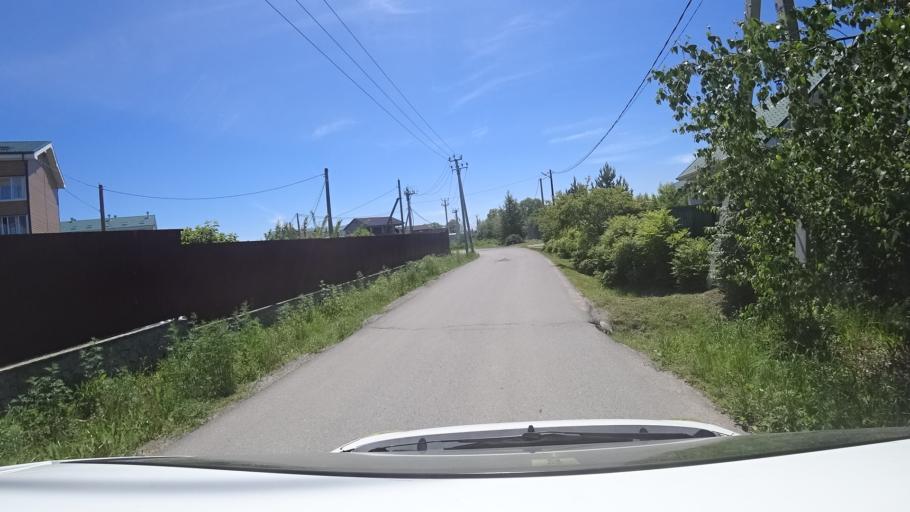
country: RU
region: Khabarovsk Krai
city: Topolevo
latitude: 48.5014
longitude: 135.1785
